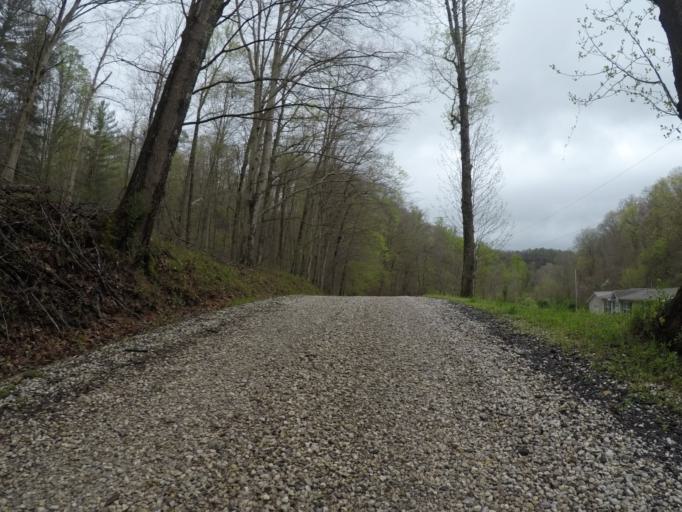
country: US
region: Ohio
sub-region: Lawrence County
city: Burlington
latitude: 38.3791
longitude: -82.4897
